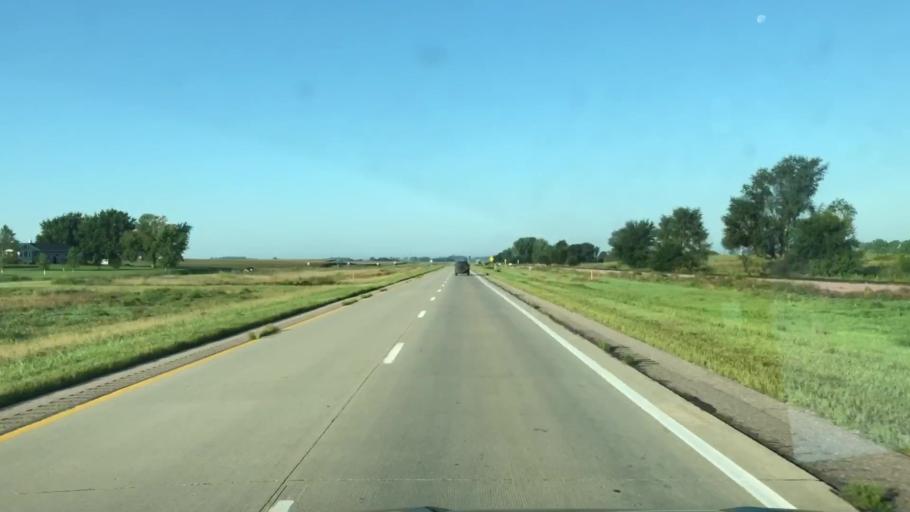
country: US
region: Iowa
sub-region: Sioux County
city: Alton
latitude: 43.0280
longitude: -95.9381
